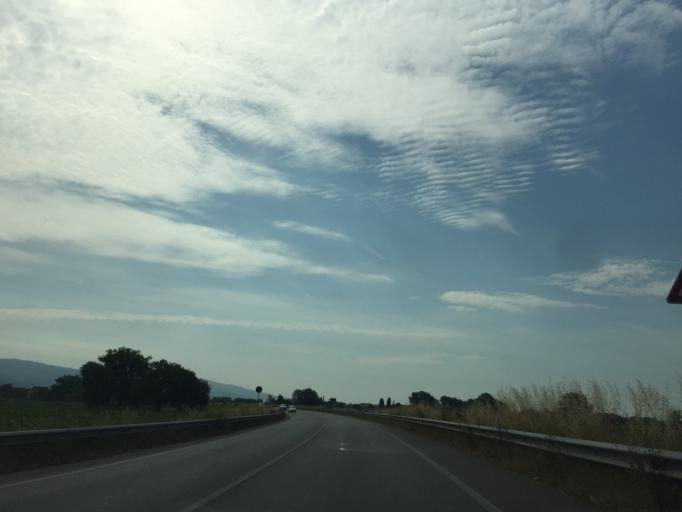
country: IT
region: Tuscany
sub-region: Provincia di Pistoia
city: Uggia-Pazzera-Bizzarrino
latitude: 43.8295
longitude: 10.8305
